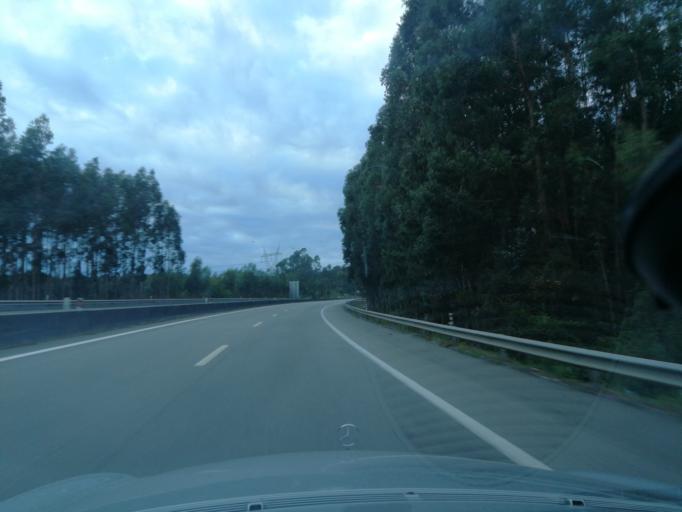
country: PT
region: Aveiro
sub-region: Albergaria-A-Velha
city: Albergaria-a-Velha
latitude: 40.6820
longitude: -8.4959
